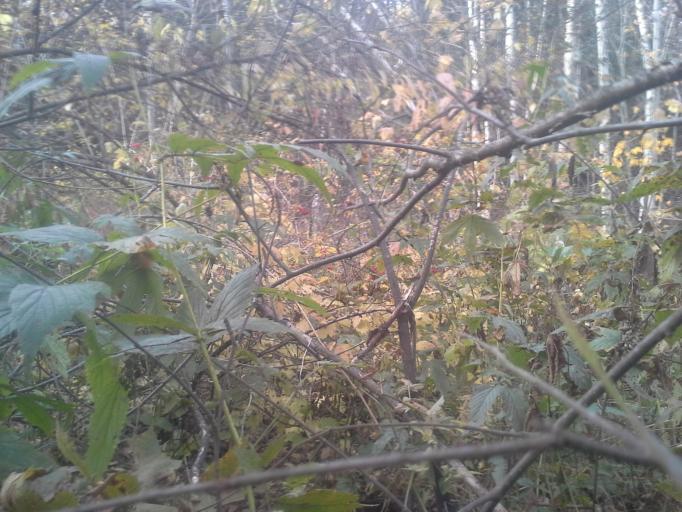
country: RU
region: Moskovskaya
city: Krasnoznamensk
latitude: 55.5801
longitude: 37.0273
